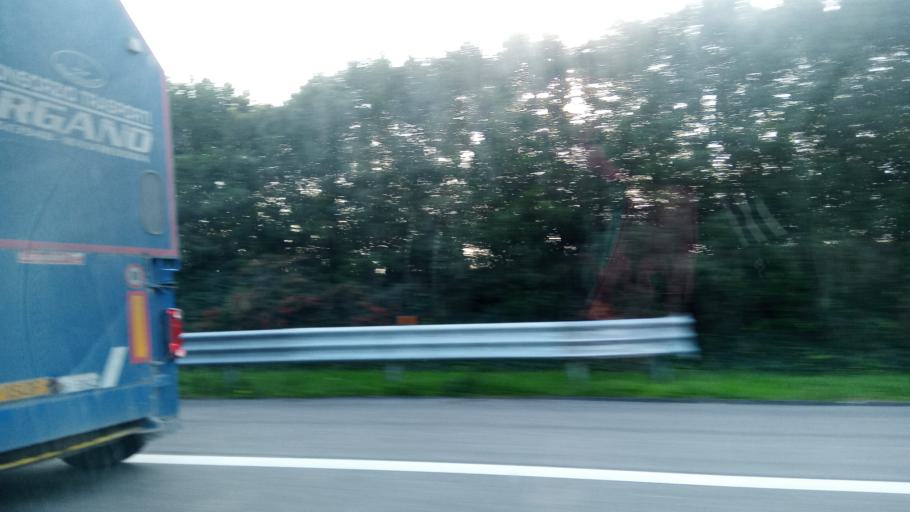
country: IT
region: Molise
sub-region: Provincia di Campobasso
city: Campomarino
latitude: 41.9455
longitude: 15.0293
